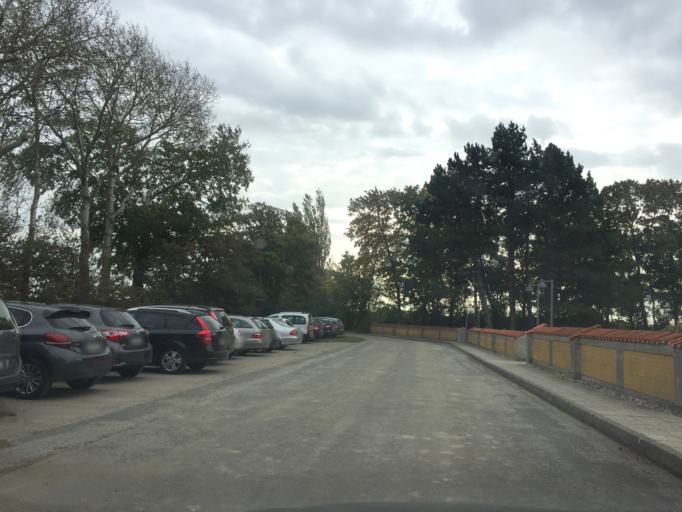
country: DK
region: Zealand
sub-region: Lolland Kommune
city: Rodbyhavn
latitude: 54.6682
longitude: 11.3398
